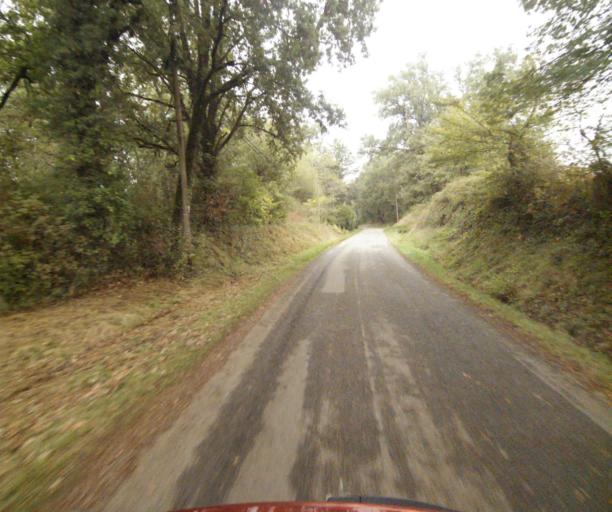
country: FR
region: Midi-Pyrenees
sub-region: Departement du Tarn-et-Garonne
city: Verdun-sur-Garonne
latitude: 43.8360
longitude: 1.1952
